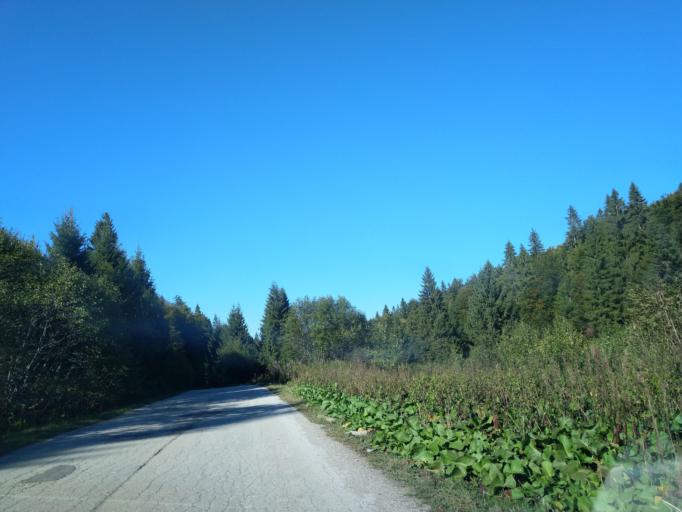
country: RS
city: Sokolovica
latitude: 43.3575
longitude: 20.2558
